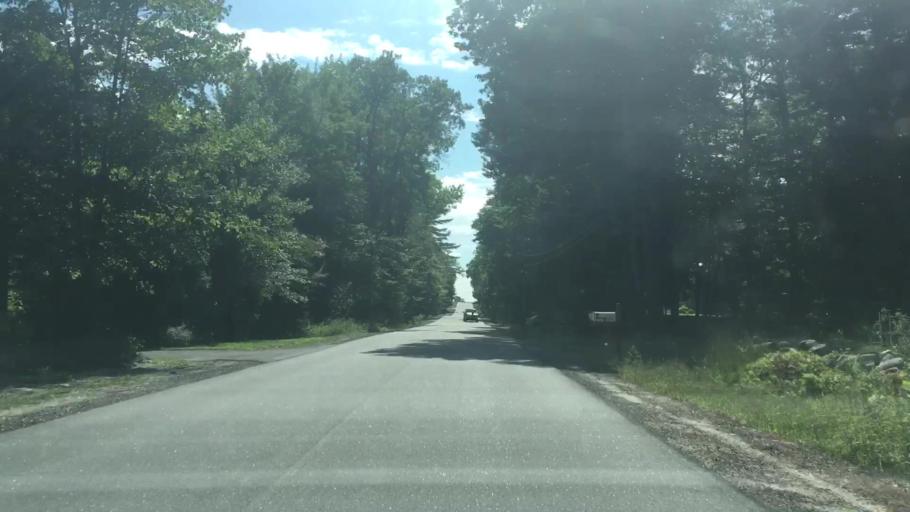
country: US
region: Maine
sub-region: Androscoggin County
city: Poland
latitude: 44.0082
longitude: -70.3682
